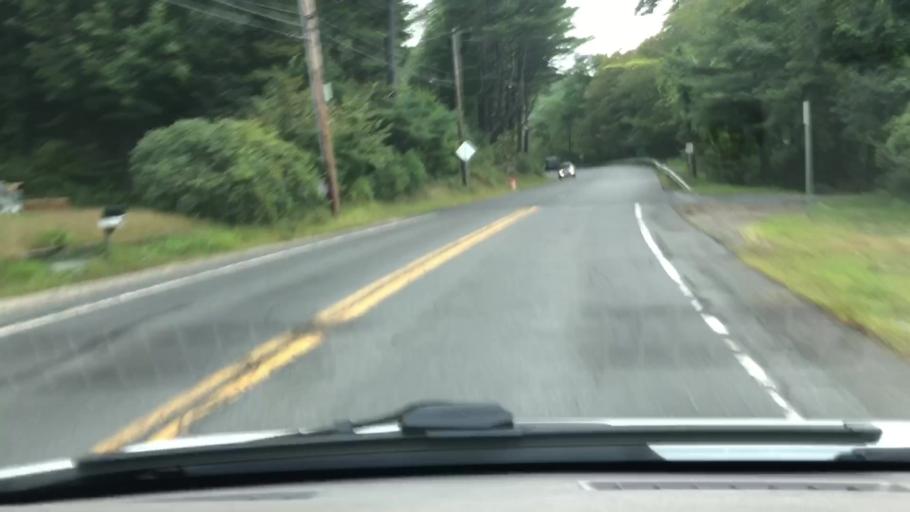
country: US
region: Massachusetts
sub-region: Franklin County
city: Charlemont
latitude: 42.6278
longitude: -72.8628
